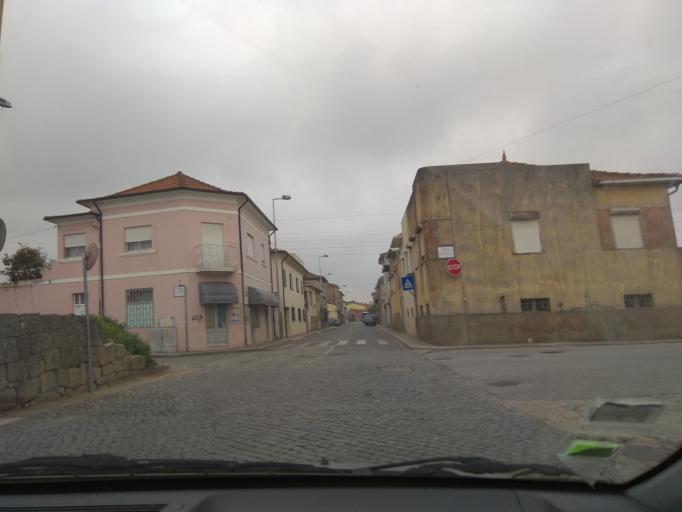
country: PT
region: Porto
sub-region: Matosinhos
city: Guifoes
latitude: 41.1960
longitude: -8.6628
